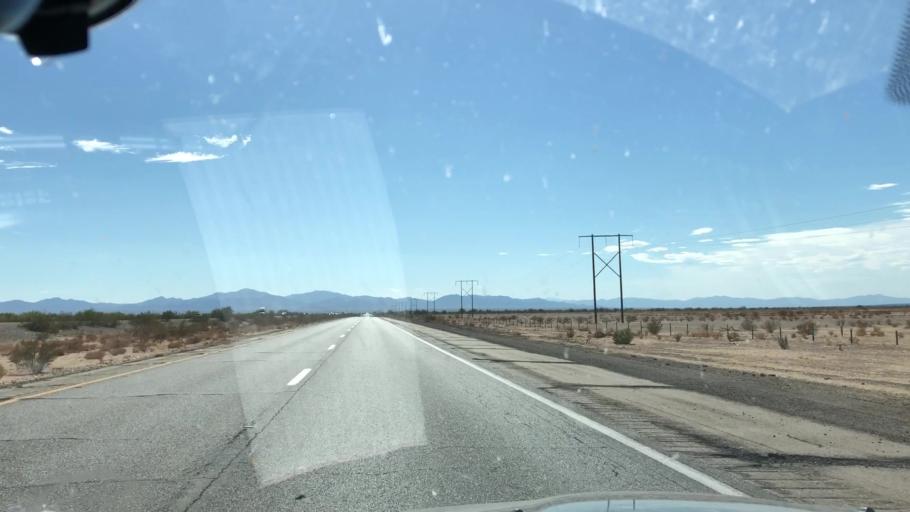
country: US
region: California
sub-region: Riverside County
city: Mesa Verde
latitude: 33.6063
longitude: -114.9594
